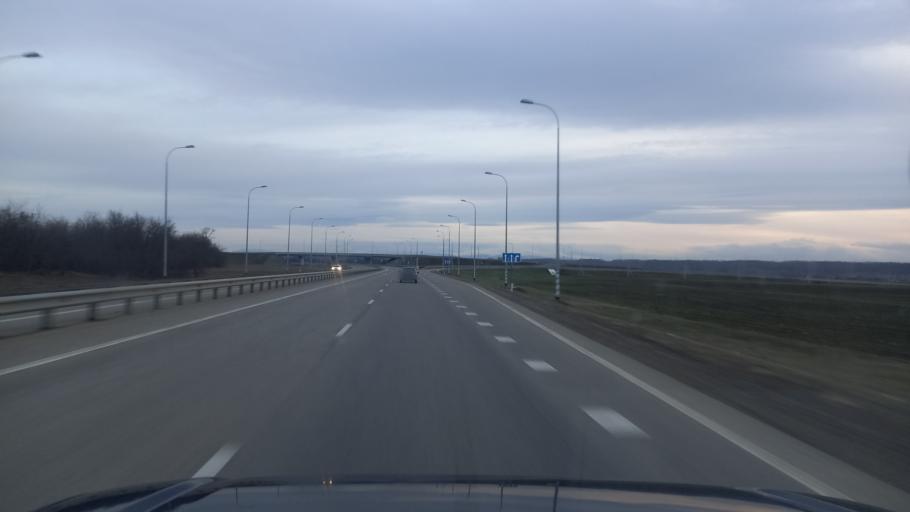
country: RU
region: Adygeya
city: Khanskaya
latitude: 44.6639
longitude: 39.9935
